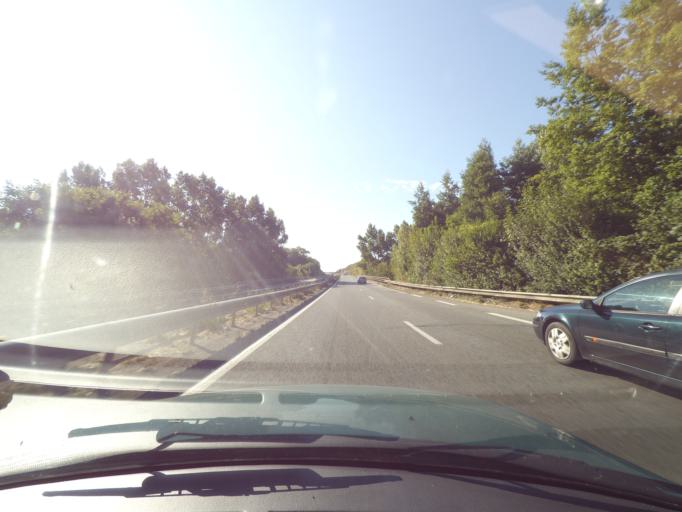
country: FR
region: Poitou-Charentes
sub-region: Departement de la Vienne
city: Migne-Auxances
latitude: 46.6265
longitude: 0.2979
